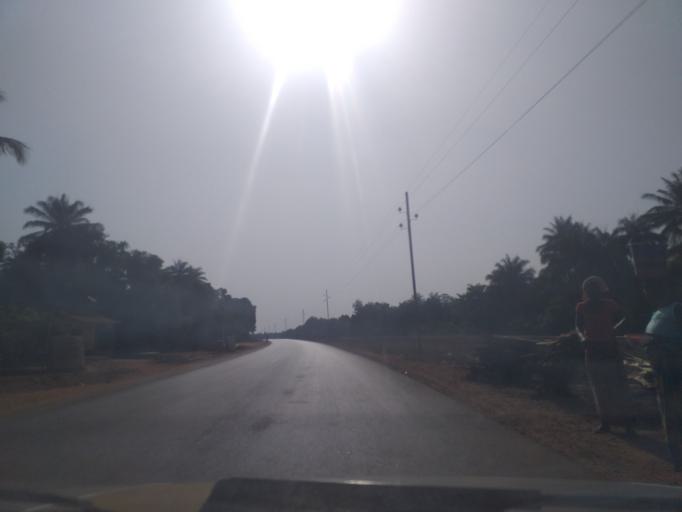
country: GN
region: Boke
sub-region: Boke Prefecture
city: Sangueya
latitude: 10.7774
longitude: -14.4377
